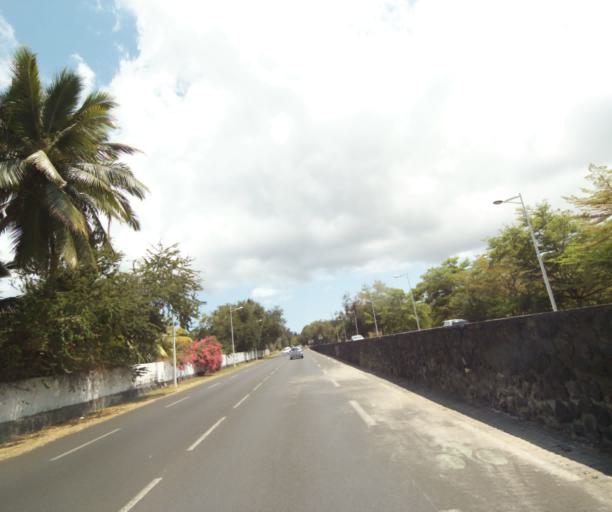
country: RE
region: Reunion
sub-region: Reunion
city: Trois-Bassins
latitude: -21.0780
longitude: 55.2286
